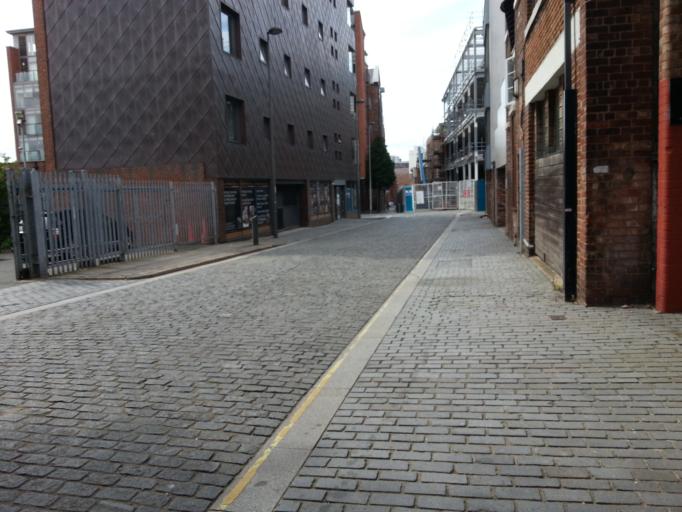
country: GB
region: England
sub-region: Liverpool
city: Liverpool
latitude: 53.4009
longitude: -2.9803
